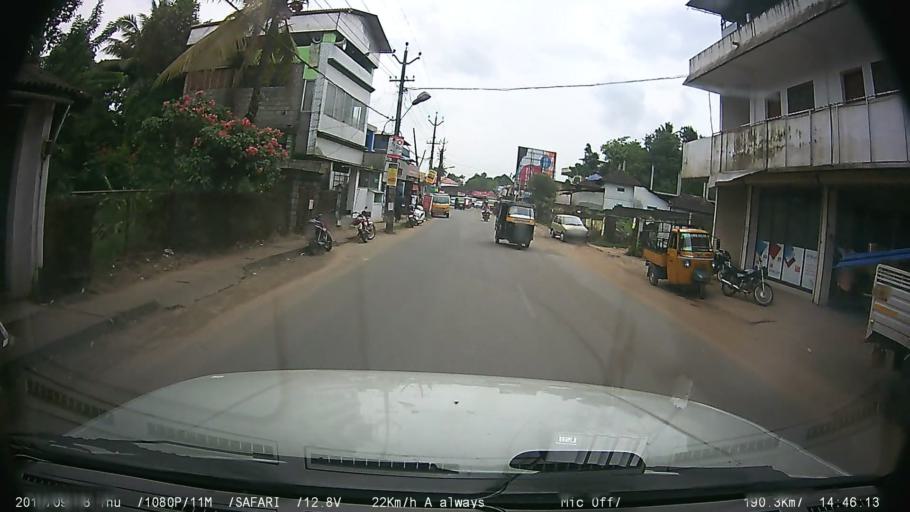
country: IN
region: Kerala
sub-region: Ernakulam
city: Muvattupula
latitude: 9.9926
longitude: 76.5859
